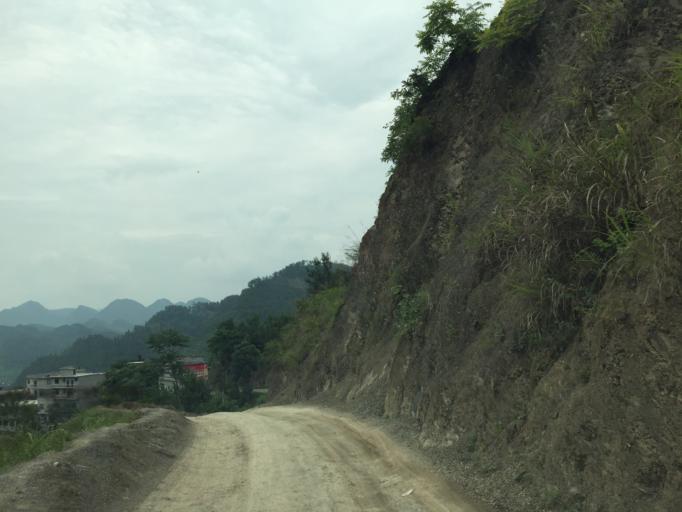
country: CN
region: Guizhou Sheng
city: Tongjing
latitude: 28.3716
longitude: 108.2563
